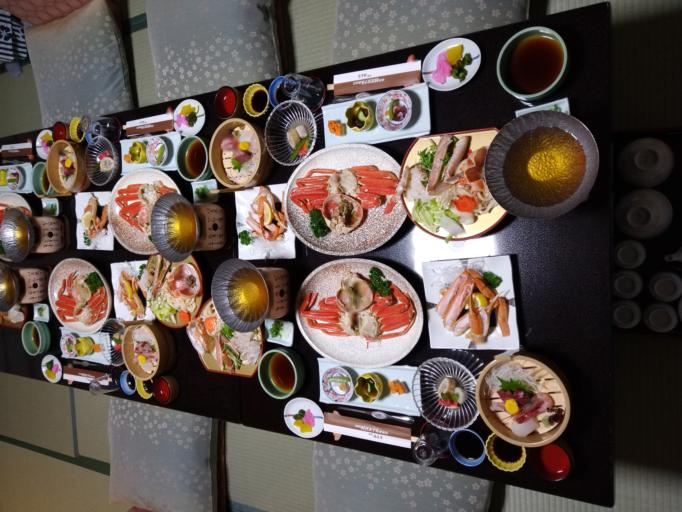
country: JP
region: Hyogo
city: Toyooka
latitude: 35.6271
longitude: 134.8143
